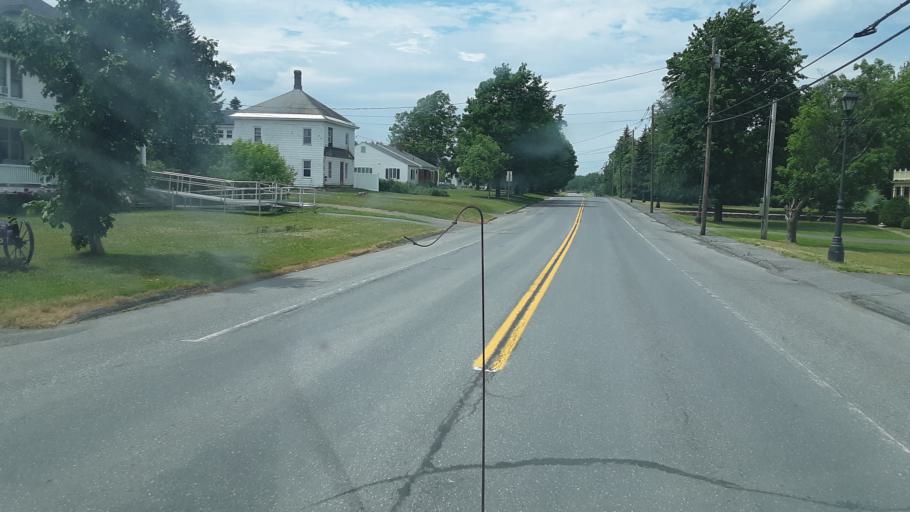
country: US
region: Maine
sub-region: Aroostook County
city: Fort Fairfield
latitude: 46.7738
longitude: -67.8376
